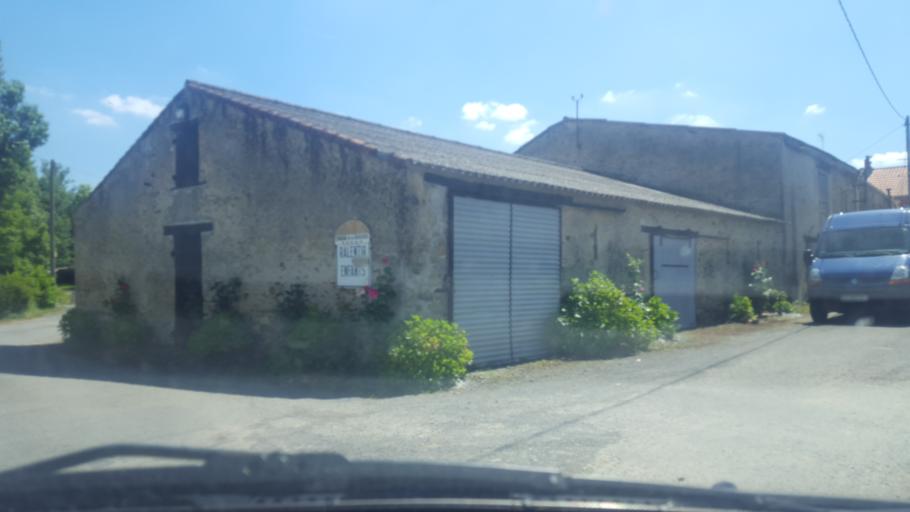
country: FR
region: Pays de la Loire
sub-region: Departement de la Loire-Atlantique
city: La Limouziniere
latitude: 47.0155
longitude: -1.5935
